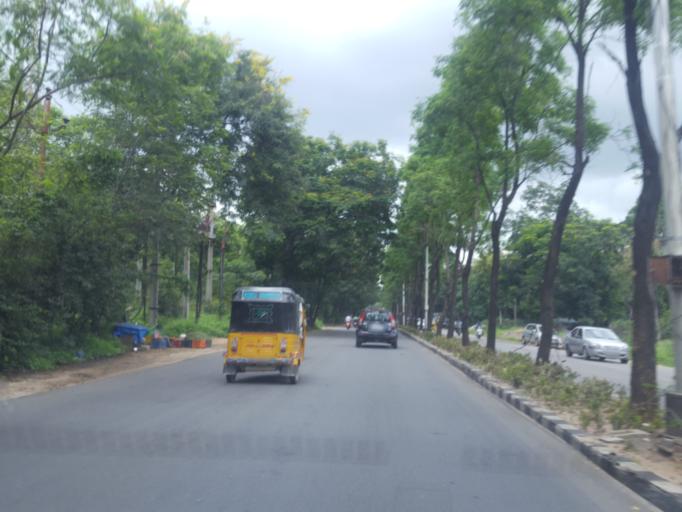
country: IN
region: Telangana
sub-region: Medak
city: Serilingampalle
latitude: 17.4578
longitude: 78.3390
